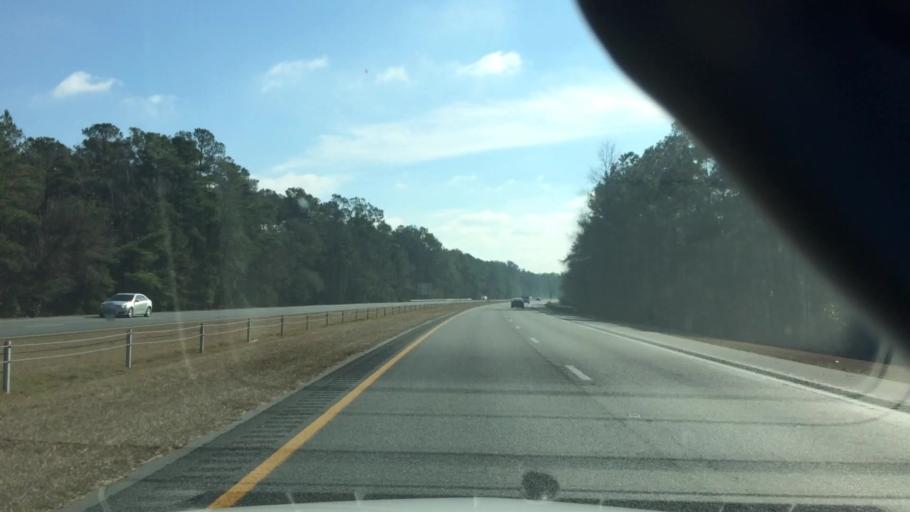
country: US
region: North Carolina
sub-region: Duplin County
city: Wallace
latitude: 34.7481
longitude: -77.9457
